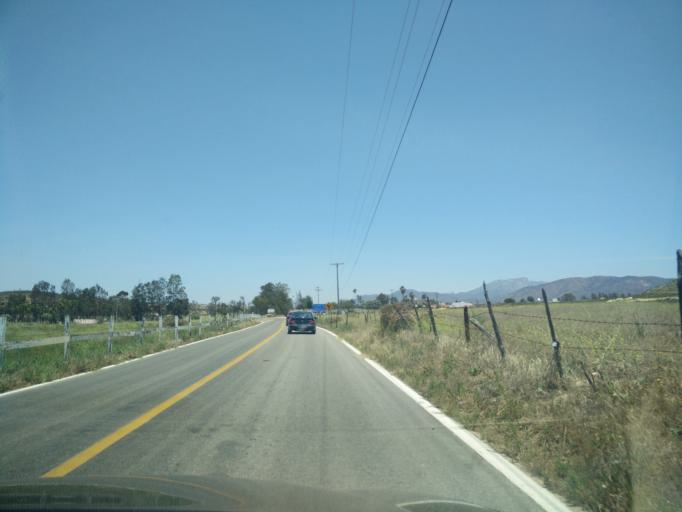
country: MX
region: Baja California
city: El Sauzal
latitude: 32.0116
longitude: -116.6741
